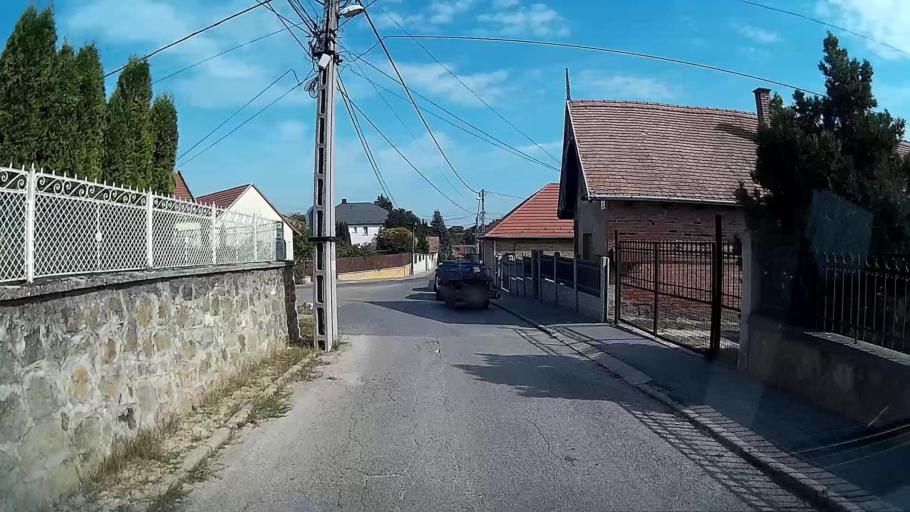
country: HU
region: Pest
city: Solymar
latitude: 47.5896
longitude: 18.9319
